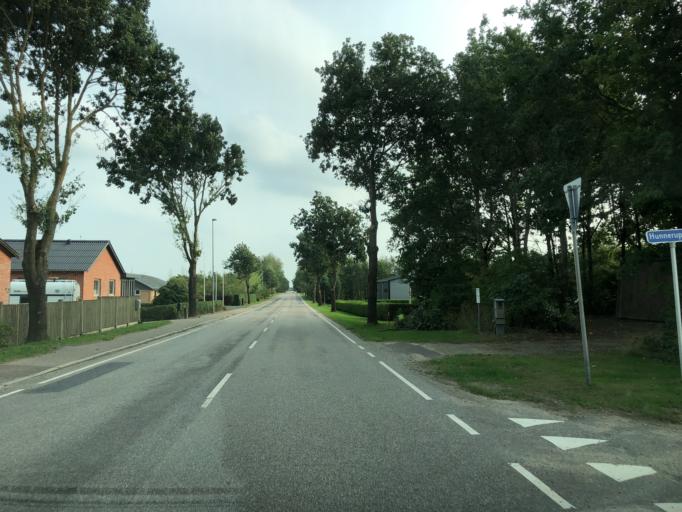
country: DK
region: Central Jutland
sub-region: Ringkobing-Skjern Kommune
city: Videbaek
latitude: 56.0965
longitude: 8.7027
